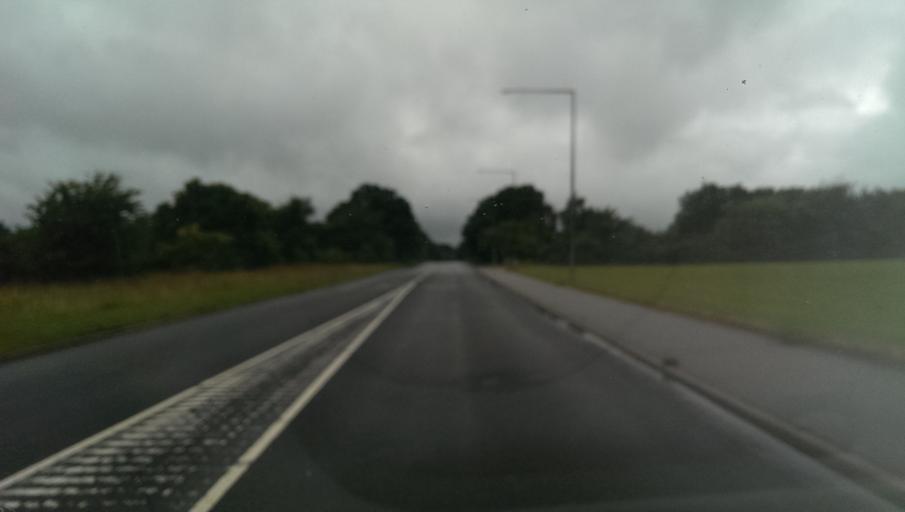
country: DK
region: South Denmark
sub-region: Esbjerg Kommune
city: Esbjerg
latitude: 55.4945
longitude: 8.4835
